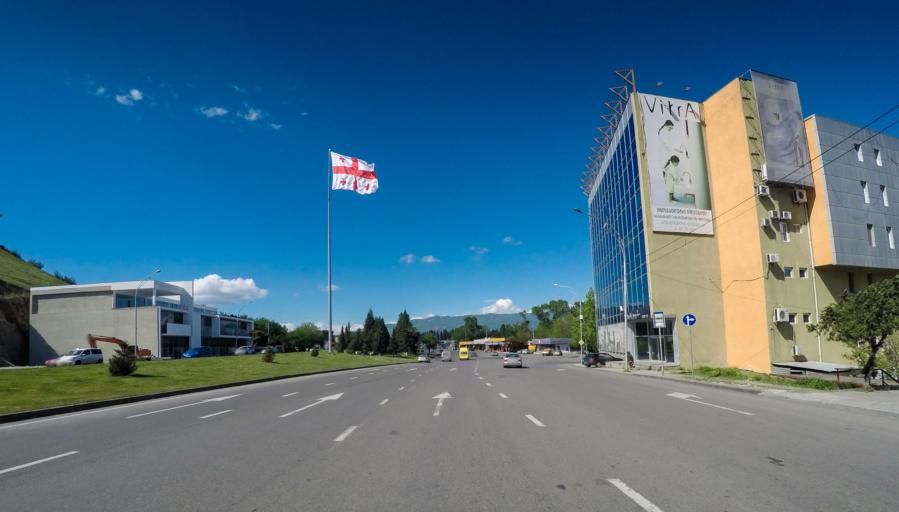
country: GE
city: Zahesi
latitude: 41.7656
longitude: 44.7690
